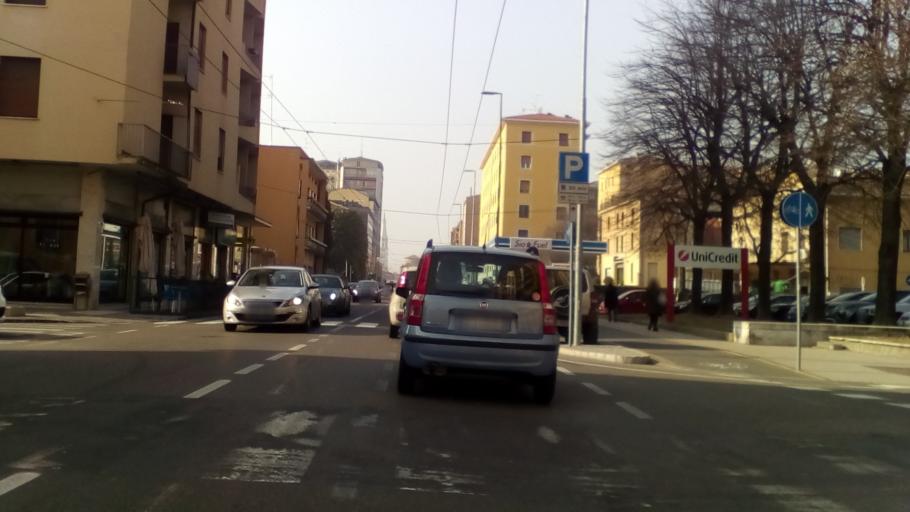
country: IT
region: Emilia-Romagna
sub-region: Provincia di Modena
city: Modena
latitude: 44.6416
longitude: 10.9373
